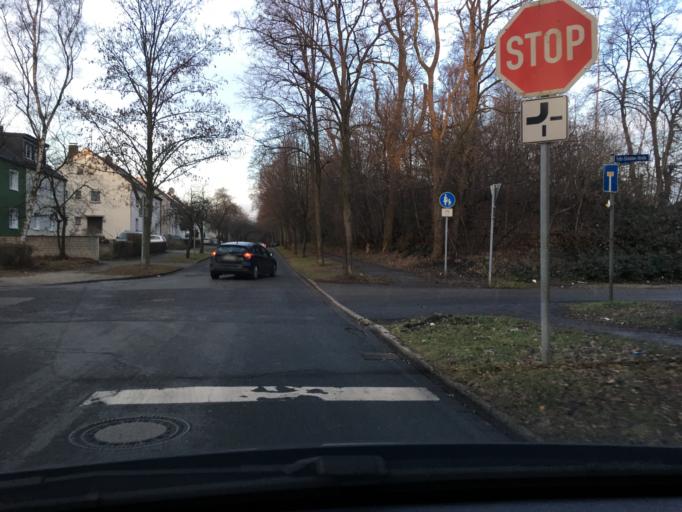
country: DE
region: North Rhine-Westphalia
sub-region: Regierungsbezirk Dusseldorf
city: Oberhausen
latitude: 51.4580
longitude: 6.8400
